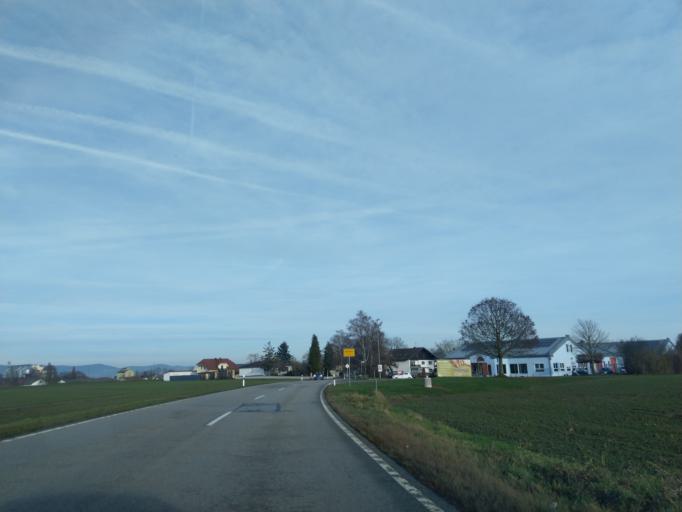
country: DE
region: Bavaria
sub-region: Lower Bavaria
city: Buchhofen
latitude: 48.6936
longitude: 12.9162
